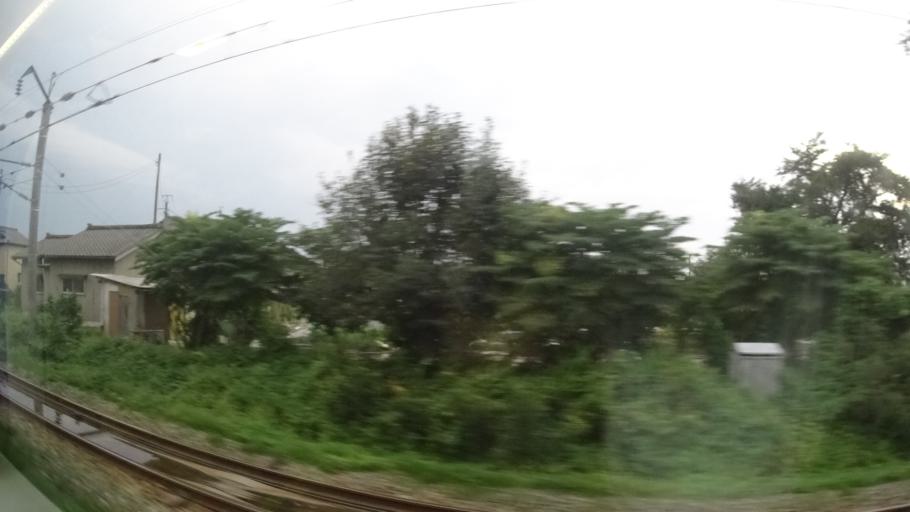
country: JP
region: Niigata
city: Murakami
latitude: 38.2308
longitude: 139.4593
